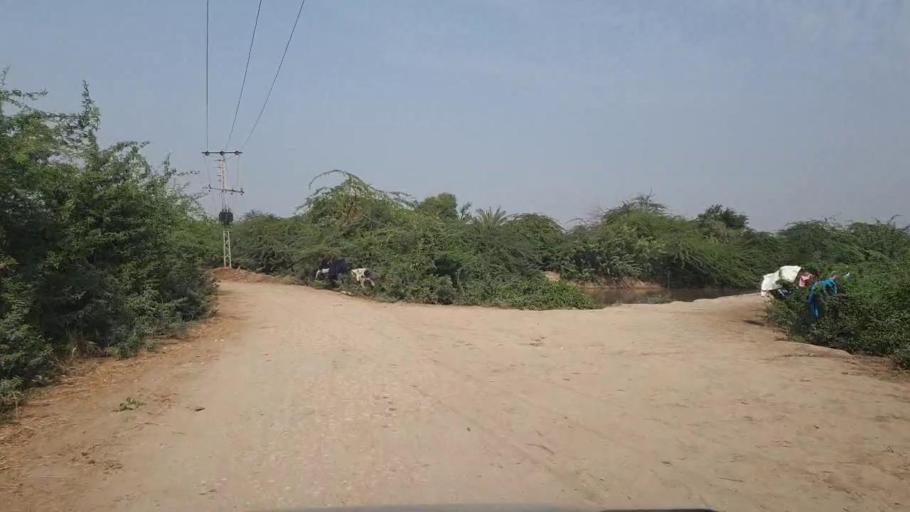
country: PK
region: Sindh
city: Tando Muhammad Khan
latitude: 25.1216
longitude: 68.3879
